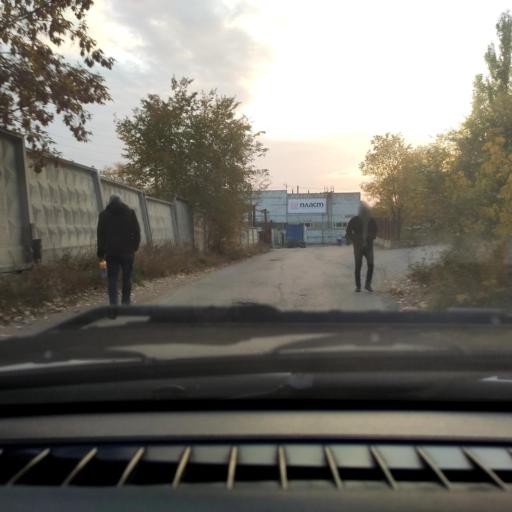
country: RU
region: Samara
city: Zhigulevsk
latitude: 53.4845
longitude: 49.4938
